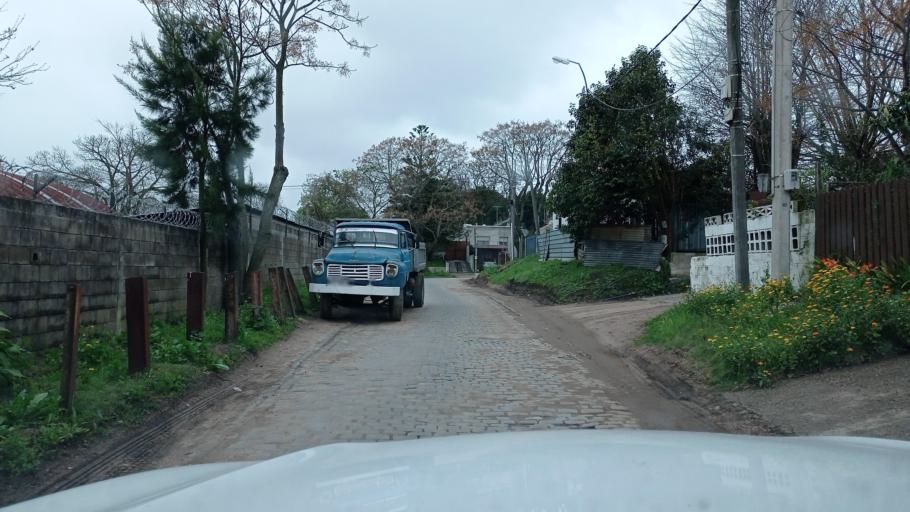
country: UY
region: Montevideo
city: Montevideo
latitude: -34.8502
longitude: -56.2152
